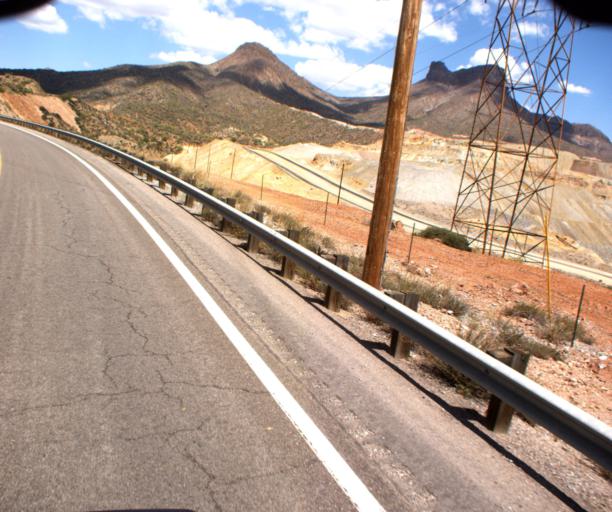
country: US
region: Arizona
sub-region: Pinal County
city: Superior
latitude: 33.1717
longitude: -111.0118
